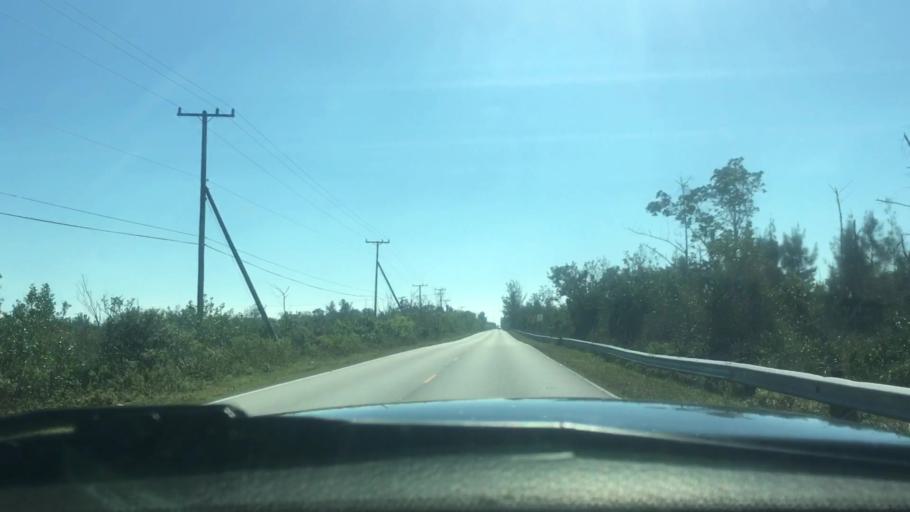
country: US
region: Florida
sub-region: Miami-Dade County
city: Florida City
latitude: 25.3744
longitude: -80.4347
